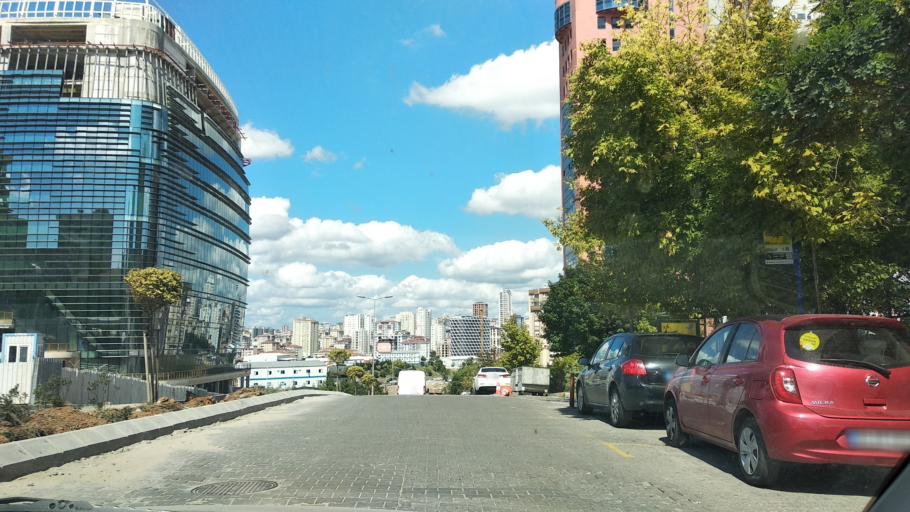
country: TR
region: Istanbul
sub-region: Atasehir
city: Atasehir
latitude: 40.9933
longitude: 29.1277
